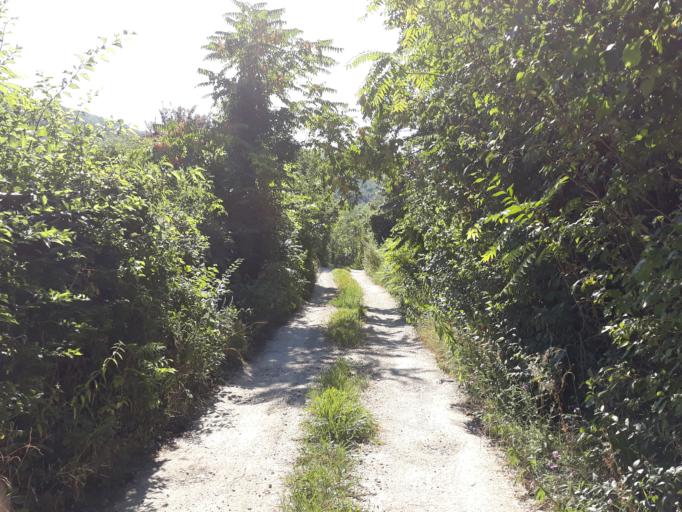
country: HU
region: Komarom-Esztergom
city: Esztergom
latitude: 47.7834
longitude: 18.7651
